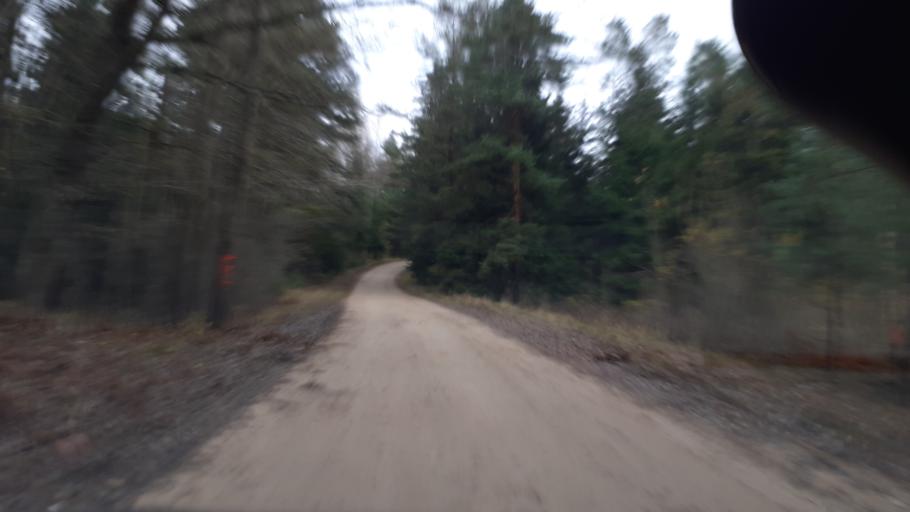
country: LV
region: Kuldigas Rajons
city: Kuldiga
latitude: 57.0329
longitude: 21.8740
